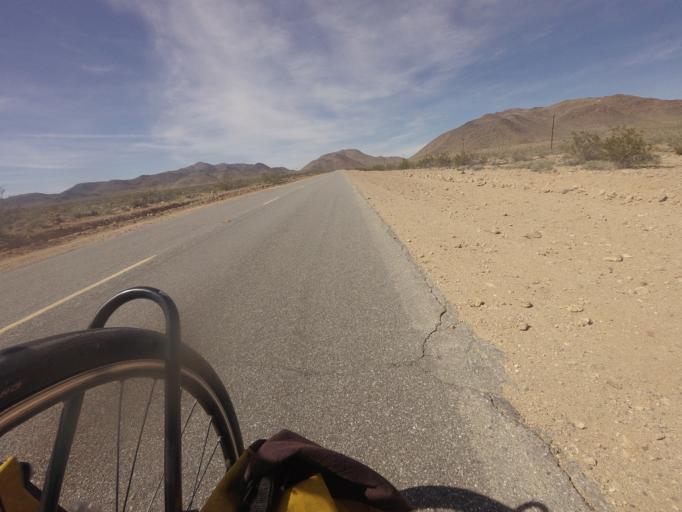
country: US
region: California
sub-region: San Bernardino County
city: Searles Valley
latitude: 35.5733
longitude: -117.4482
